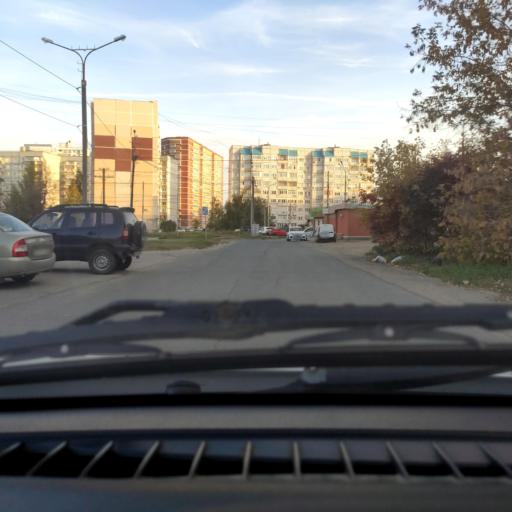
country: RU
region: Samara
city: Tol'yatti
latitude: 53.5380
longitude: 49.3969
